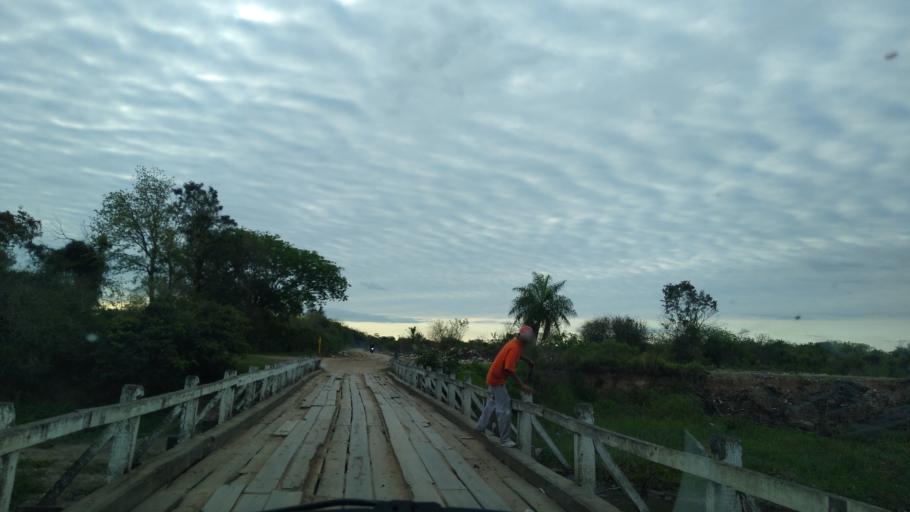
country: AR
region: Chaco
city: Fontana
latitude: -27.3977
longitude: -59.0467
